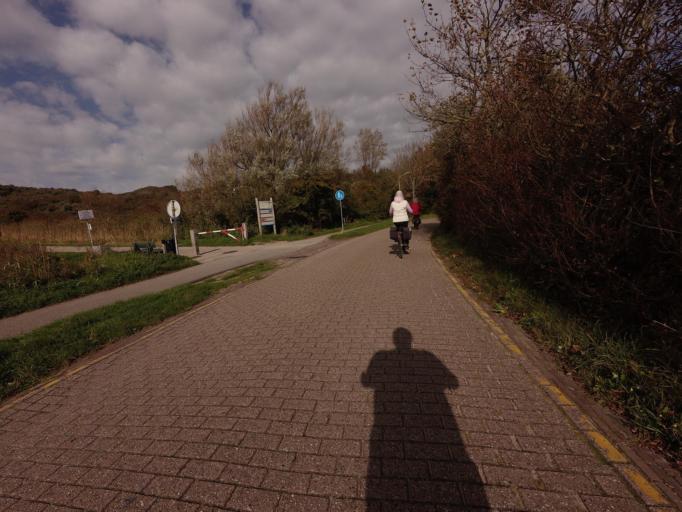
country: NL
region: Zeeland
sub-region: Gemeente Vlissingen
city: Vlissingen
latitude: 51.4970
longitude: 3.4978
